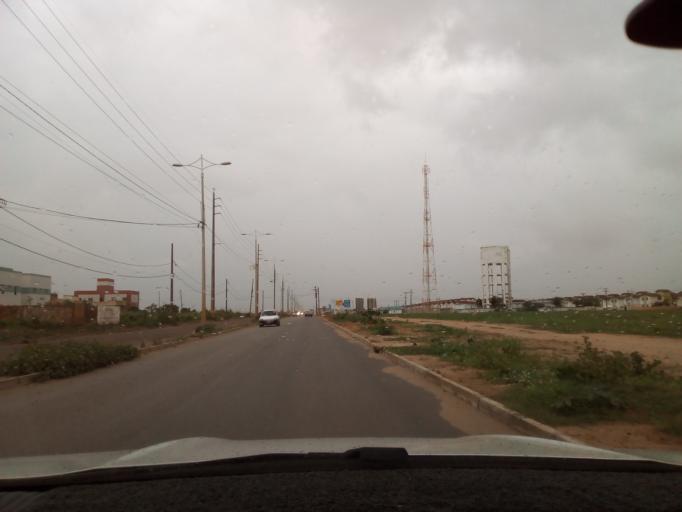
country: BR
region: Paraiba
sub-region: Conde
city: Conde
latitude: -7.1997
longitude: -34.8745
